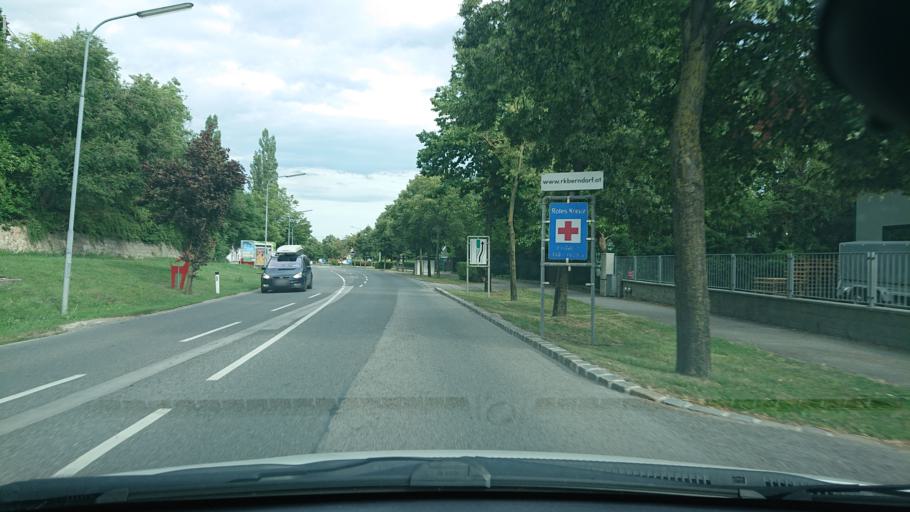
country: AT
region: Lower Austria
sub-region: Politischer Bezirk Baden
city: Berndorf
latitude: 47.9402
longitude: 16.1384
